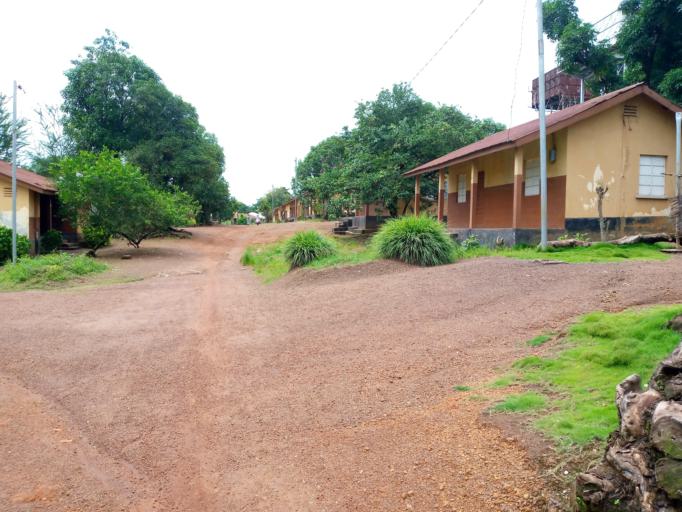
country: SL
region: Northern Province
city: Magburaka
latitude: 8.7219
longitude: -11.9389
